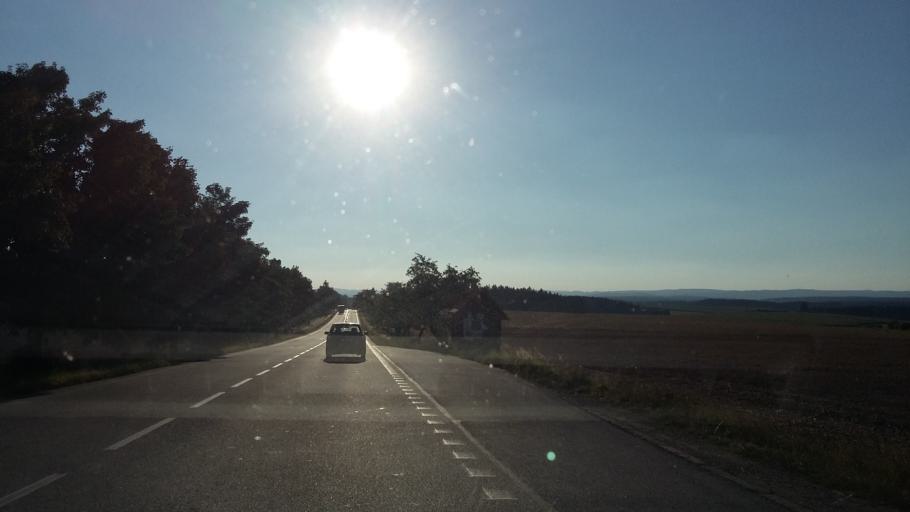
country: CZ
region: Vysocina
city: Kamenice
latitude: 49.3972
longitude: 15.7658
